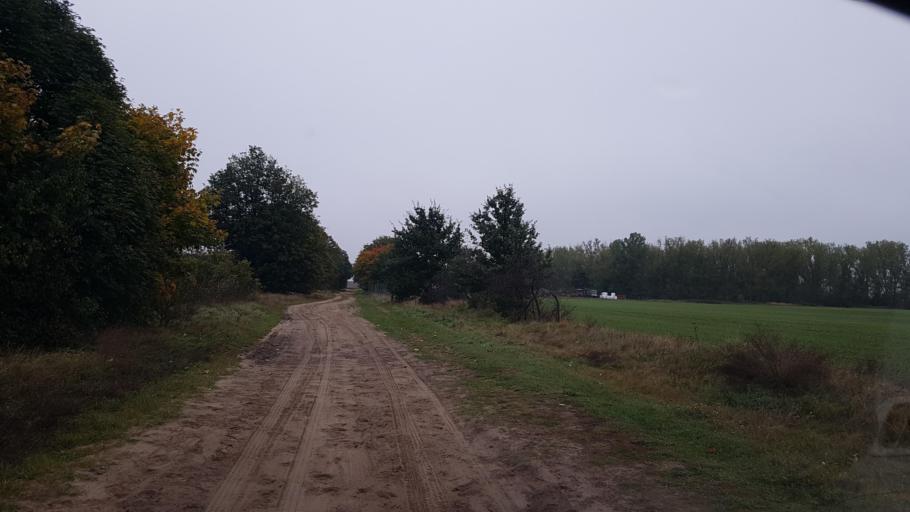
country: DE
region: Brandenburg
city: Furstenwalde
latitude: 52.4290
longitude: 14.0111
